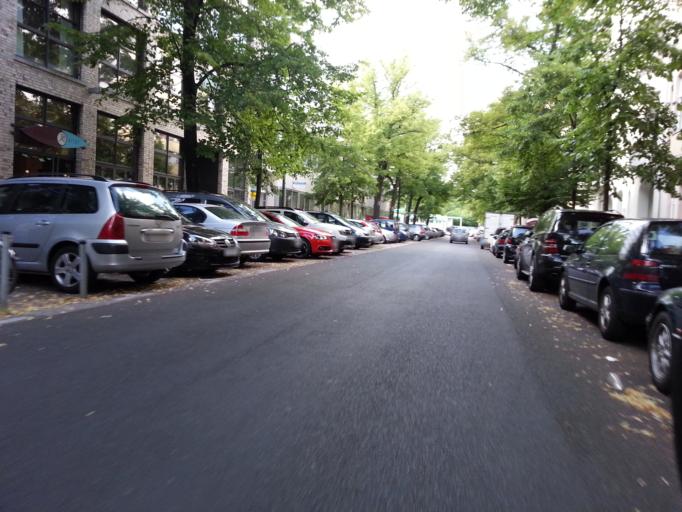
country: DE
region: Berlin
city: Halensee
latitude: 52.5005
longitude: 13.2944
